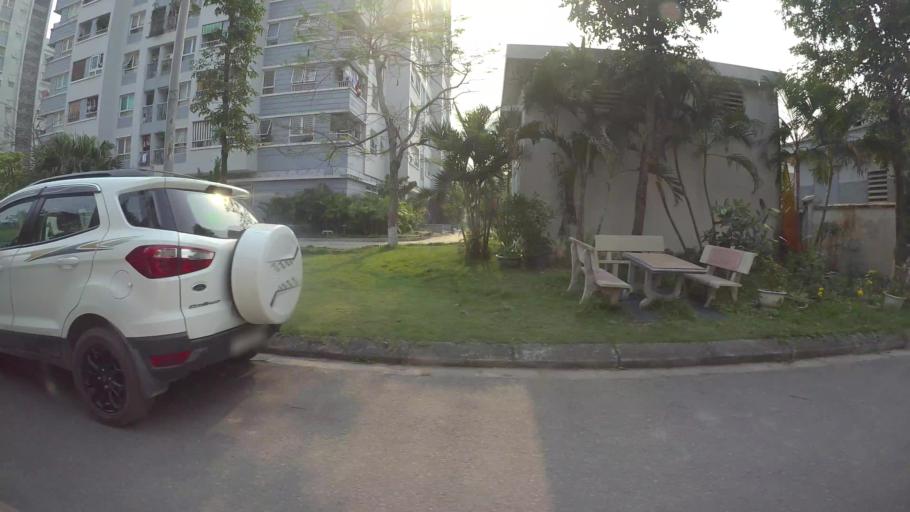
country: VN
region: Ha Noi
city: Ha Dong
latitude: 20.9972
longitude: 105.7477
